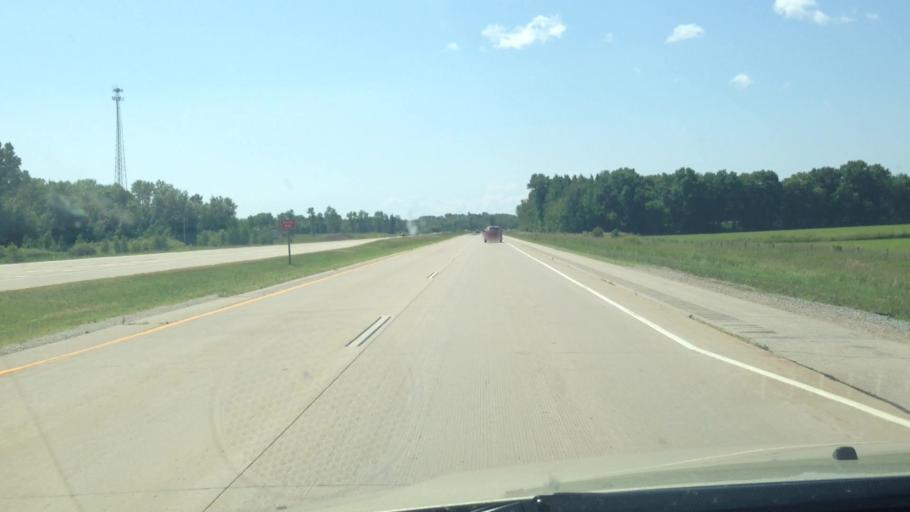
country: US
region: Wisconsin
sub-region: Oconto County
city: Oconto
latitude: 44.9352
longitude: -87.8704
